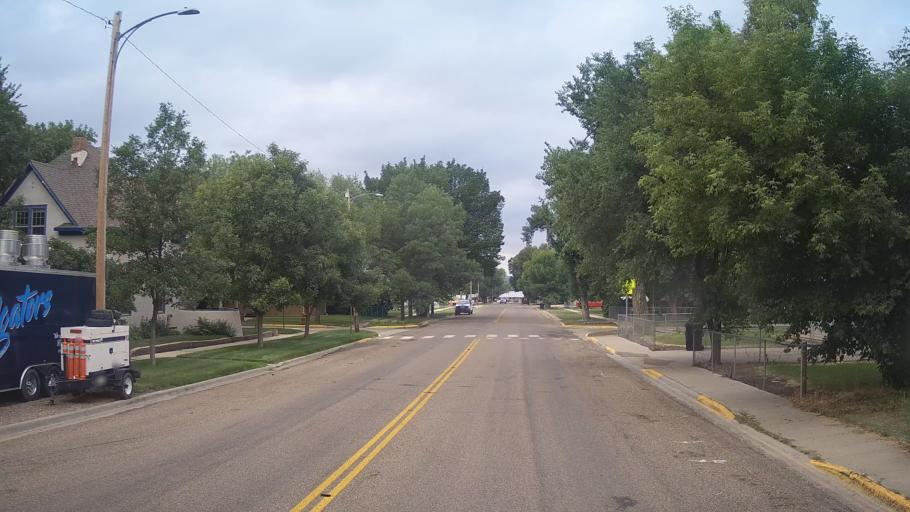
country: US
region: Montana
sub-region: Dawson County
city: Glendive
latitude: 47.0981
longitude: -104.7108
